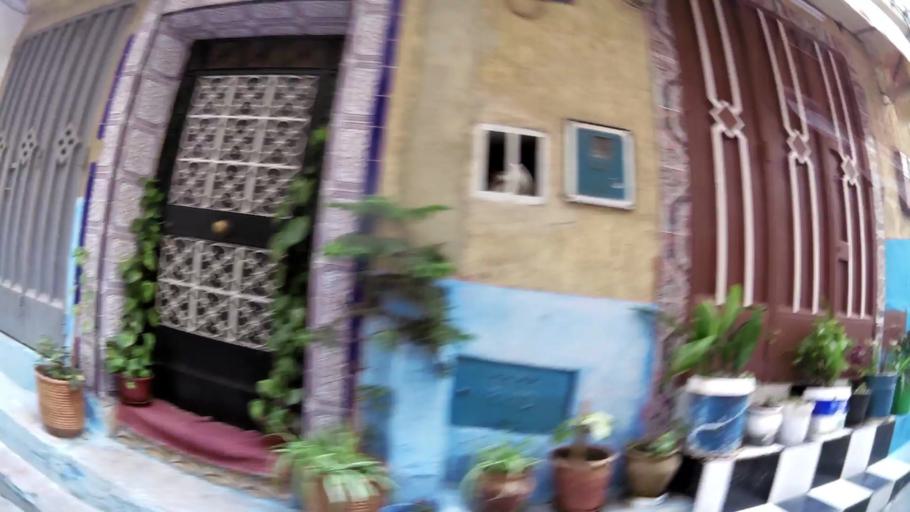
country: MA
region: Tanger-Tetouan
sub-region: Tanger-Assilah
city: Tangier
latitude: 35.7695
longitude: -5.7688
